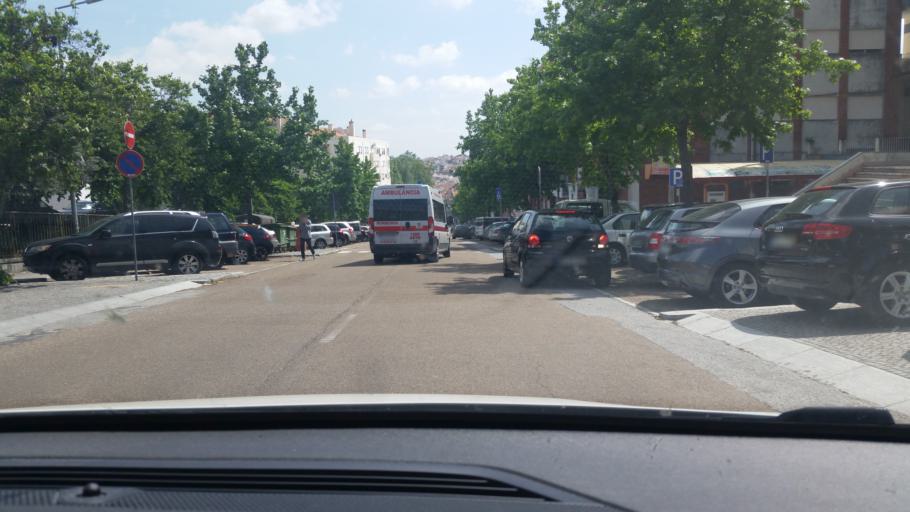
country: PT
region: Portalegre
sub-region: Portalegre
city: Portalegre
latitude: 39.3007
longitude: -7.4291
